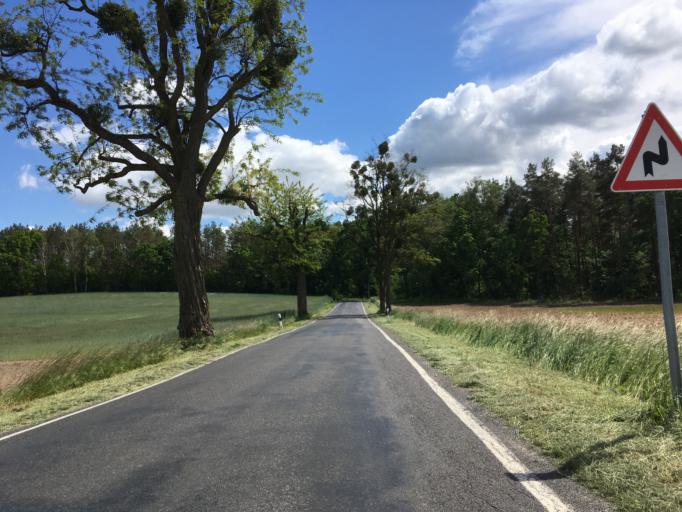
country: DE
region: Brandenburg
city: Protzel
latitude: 52.7003
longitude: 14.0201
